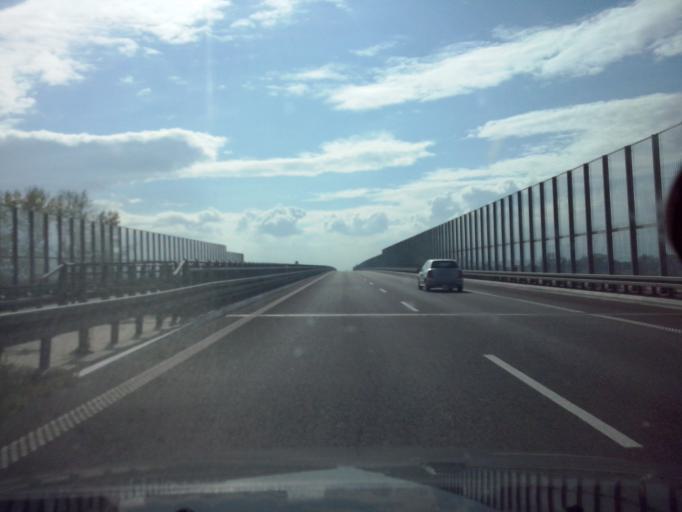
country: PL
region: Lesser Poland Voivodeship
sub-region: Powiat tarnowski
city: Niedomice
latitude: 50.0547
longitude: 20.9163
